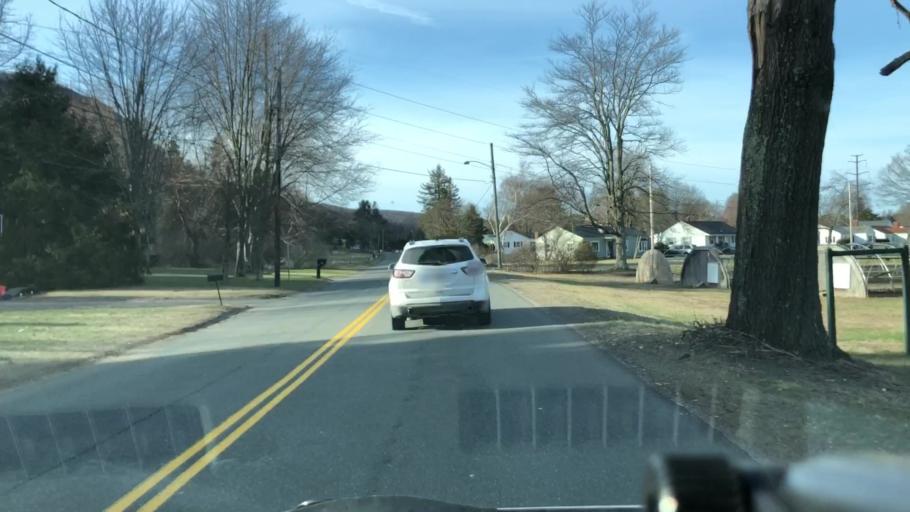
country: US
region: Massachusetts
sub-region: Hampshire County
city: Easthampton
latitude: 42.2563
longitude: -72.6522
